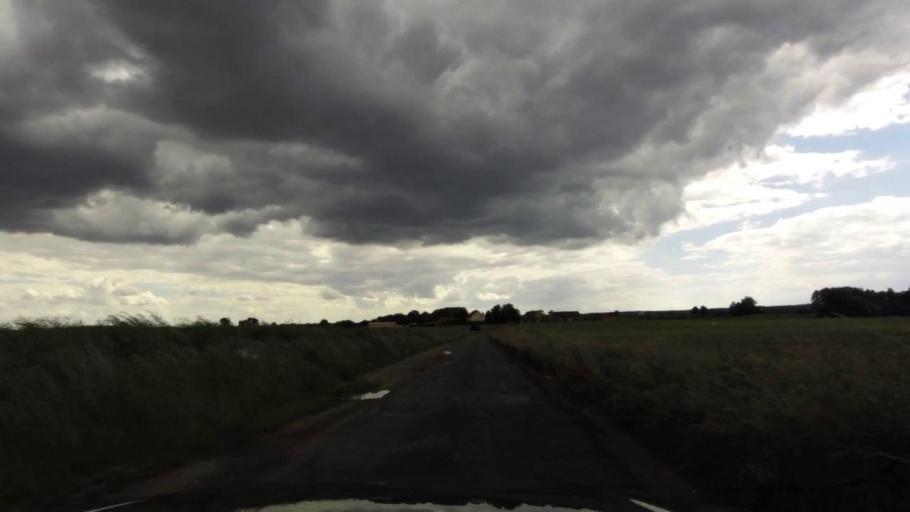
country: PL
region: West Pomeranian Voivodeship
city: Trzcinsko Zdroj
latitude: 52.9440
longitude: 14.6023
